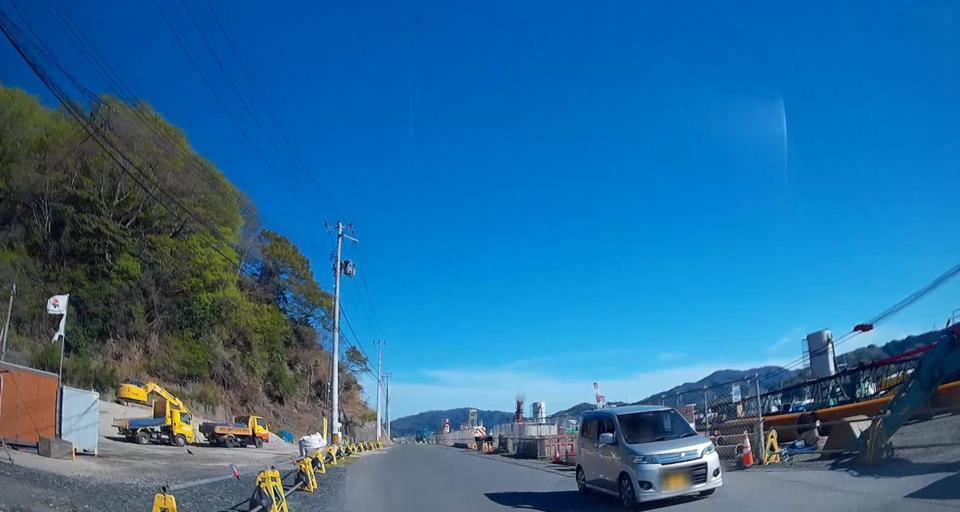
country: JP
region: Iwate
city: Kamaishi
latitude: 39.2735
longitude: 141.8934
